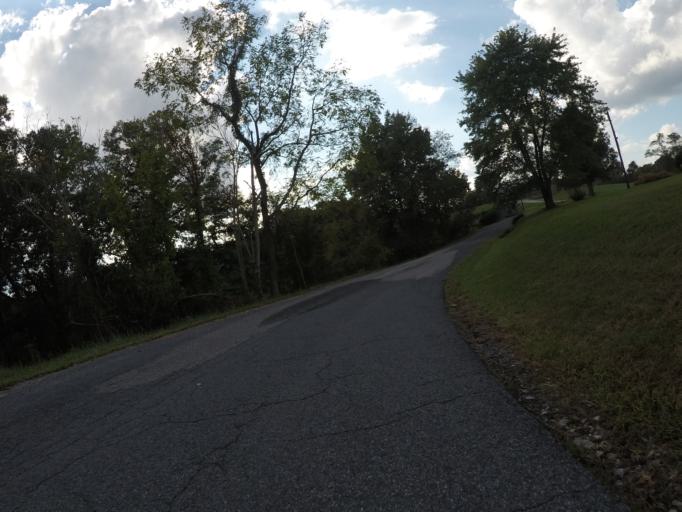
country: US
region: West Virginia
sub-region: Wayne County
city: Lavalette
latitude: 38.3601
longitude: -82.4649
